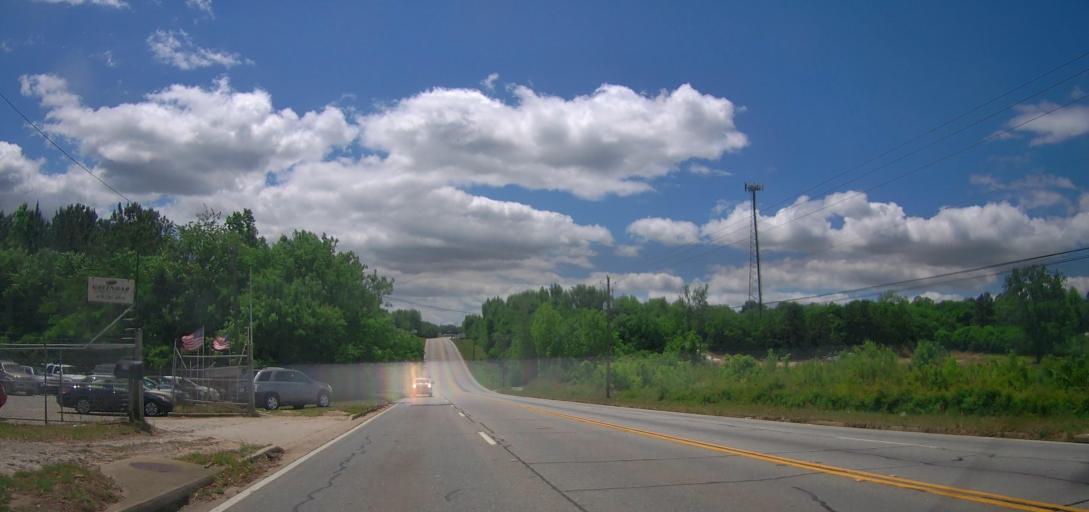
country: US
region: Georgia
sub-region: Bibb County
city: Macon
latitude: 32.8043
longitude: -83.6403
